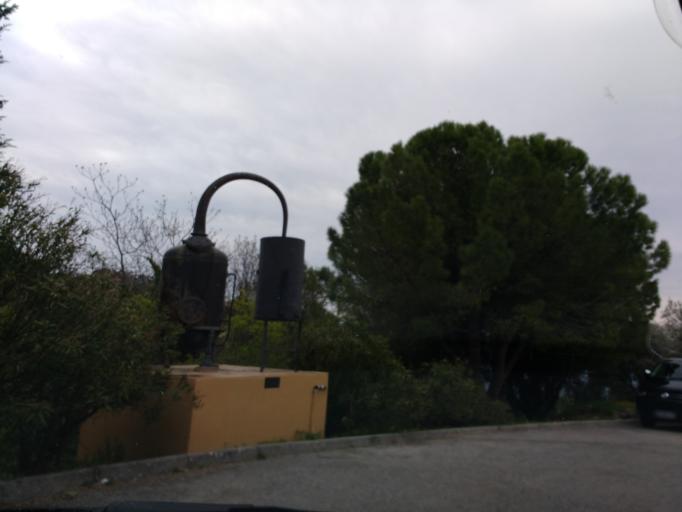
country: FR
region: Provence-Alpes-Cote d'Azur
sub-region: Departement des Alpes-Maritimes
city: Eze
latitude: 43.7300
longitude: 7.3639
